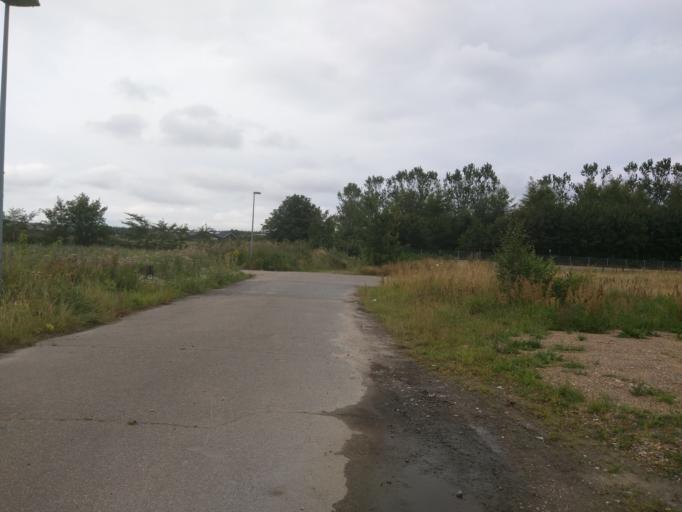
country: DK
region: Central Jutland
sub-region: Viborg Kommune
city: Viborg
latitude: 56.4542
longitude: 9.3636
